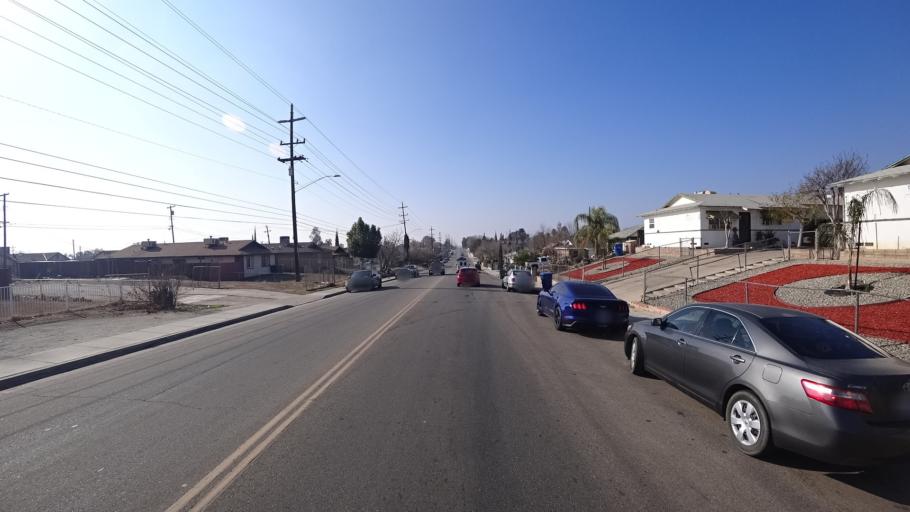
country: US
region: California
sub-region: Kern County
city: Oildale
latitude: 35.3975
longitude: -118.9881
